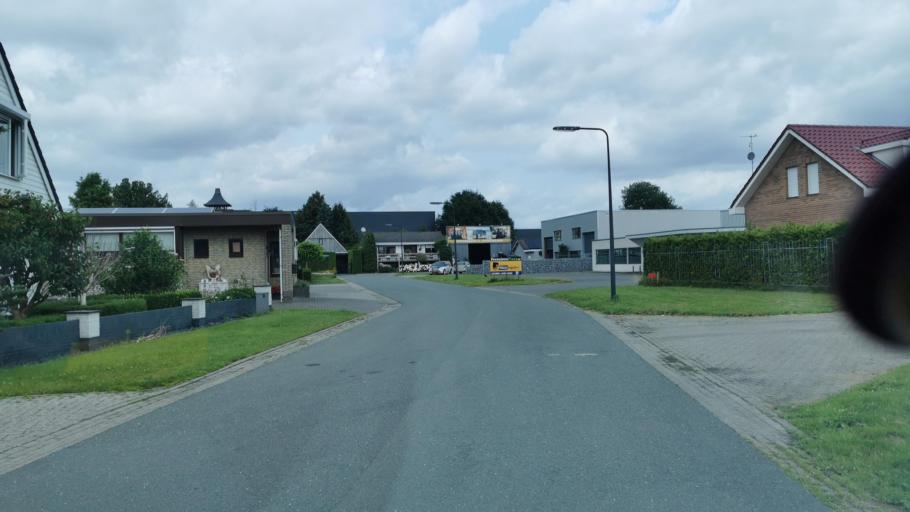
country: NL
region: Overijssel
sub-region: Gemeente Enschede
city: Enschede
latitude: 52.2243
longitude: 6.9554
